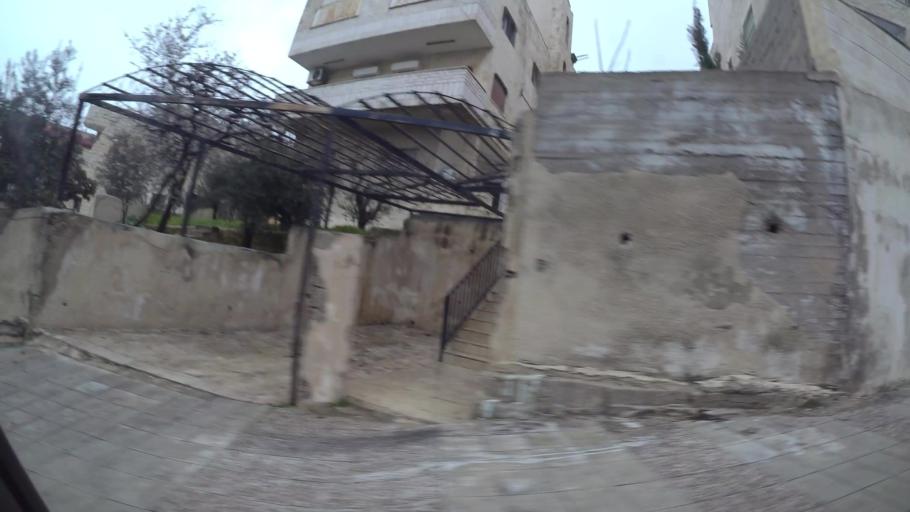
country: JO
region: Amman
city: Al Jubayhah
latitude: 32.0257
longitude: 35.8329
